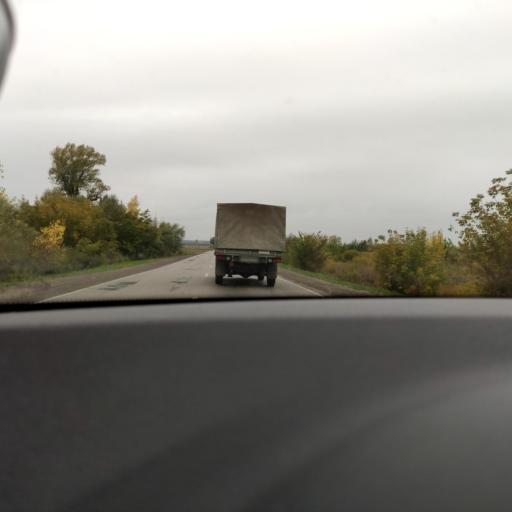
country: RU
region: Samara
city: Krasnyy Yar
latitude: 53.5034
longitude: 50.3500
